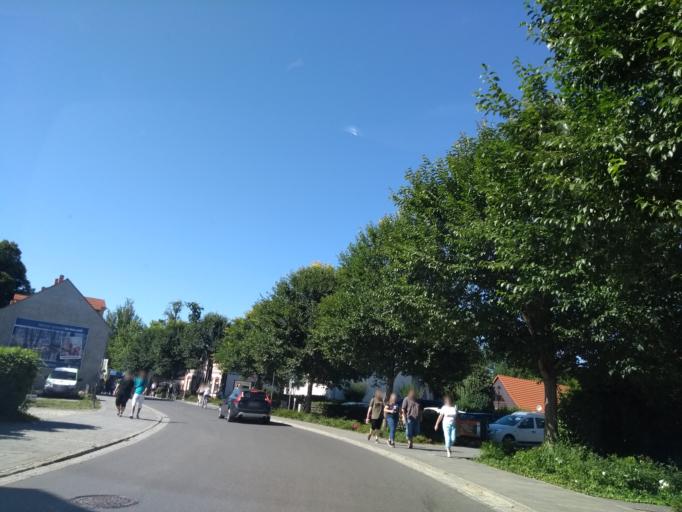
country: DE
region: Brandenburg
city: Lubbenau
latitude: 51.8659
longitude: 13.9737
